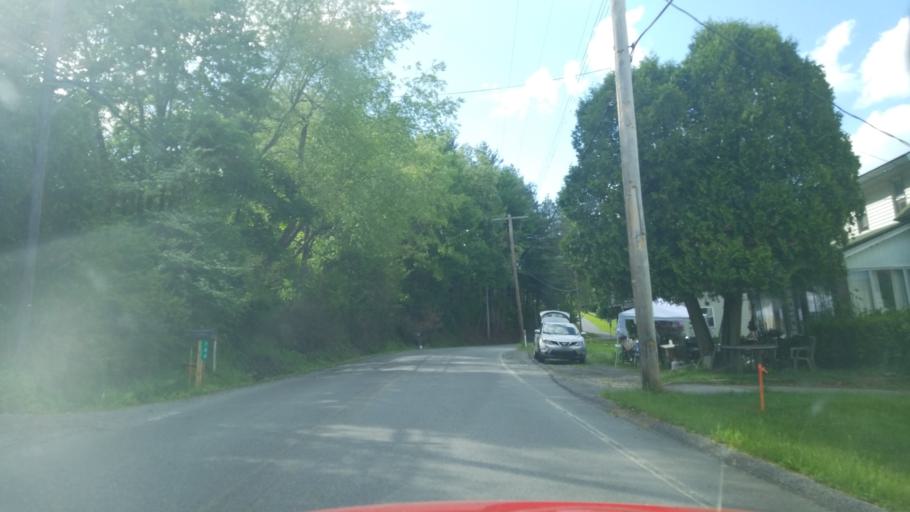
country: US
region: Pennsylvania
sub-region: Centre County
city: Philipsburg
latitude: 40.9099
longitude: -78.2464
